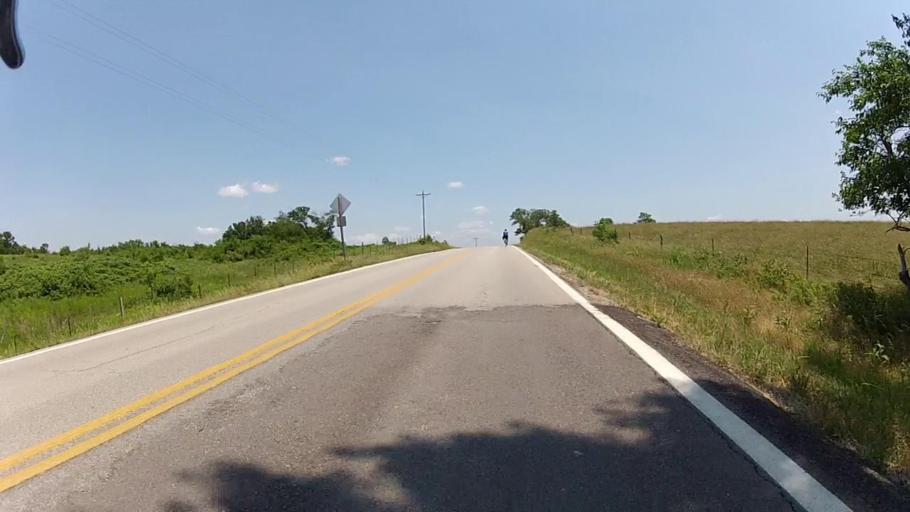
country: US
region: Kansas
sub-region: Montgomery County
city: Cherryvale
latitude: 37.1934
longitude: -95.5001
